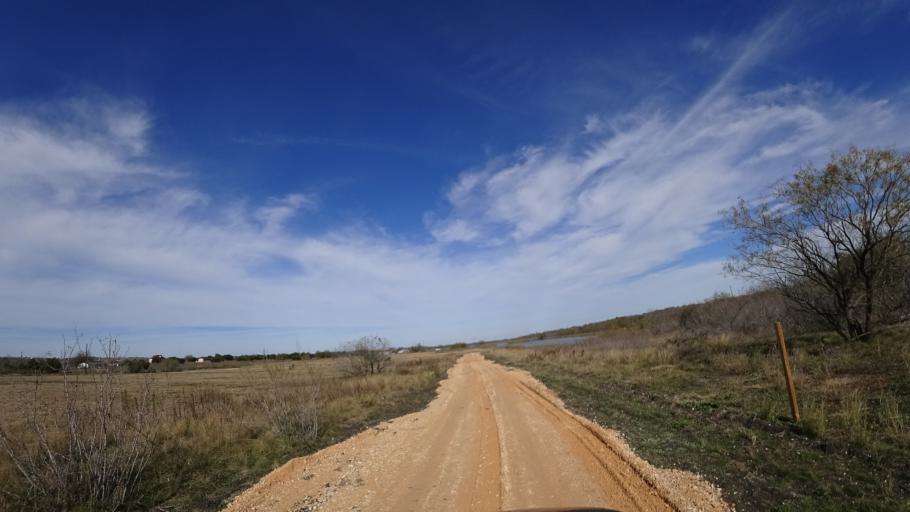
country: US
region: Texas
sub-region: Travis County
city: Onion Creek
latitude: 30.1096
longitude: -97.7162
